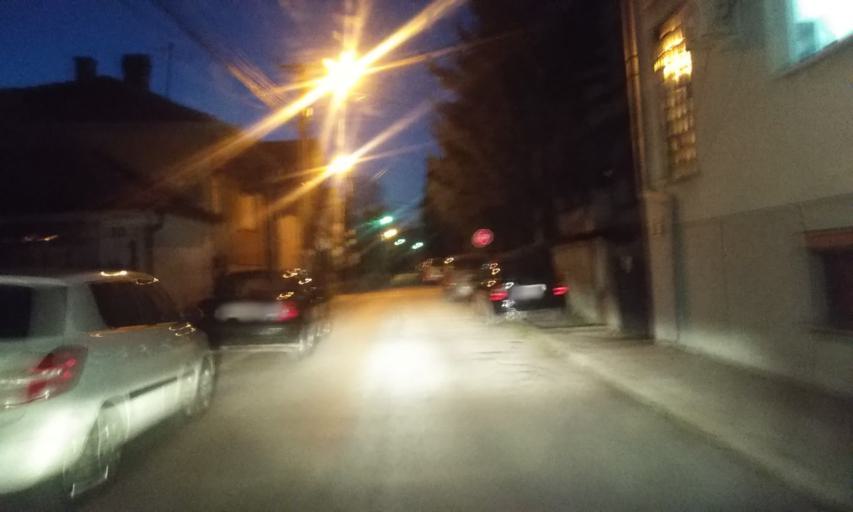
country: RS
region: Central Serbia
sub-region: Nisavski Okrug
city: Nis
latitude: 43.3302
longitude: 21.9117
